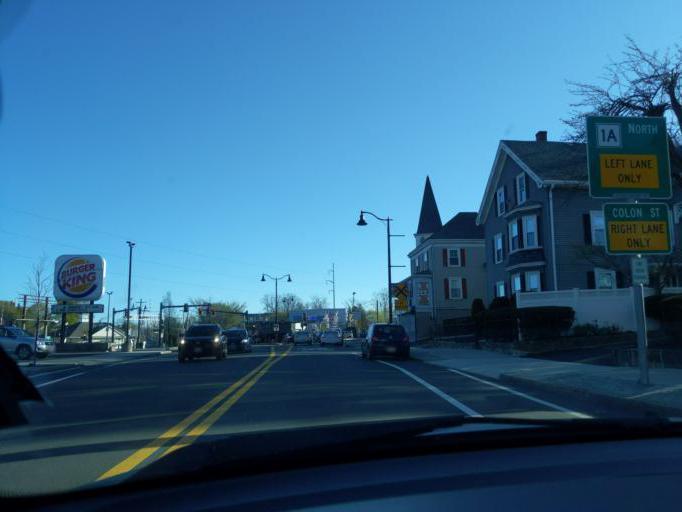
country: US
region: Massachusetts
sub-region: Essex County
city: Beverly
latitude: 42.5568
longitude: -70.8804
